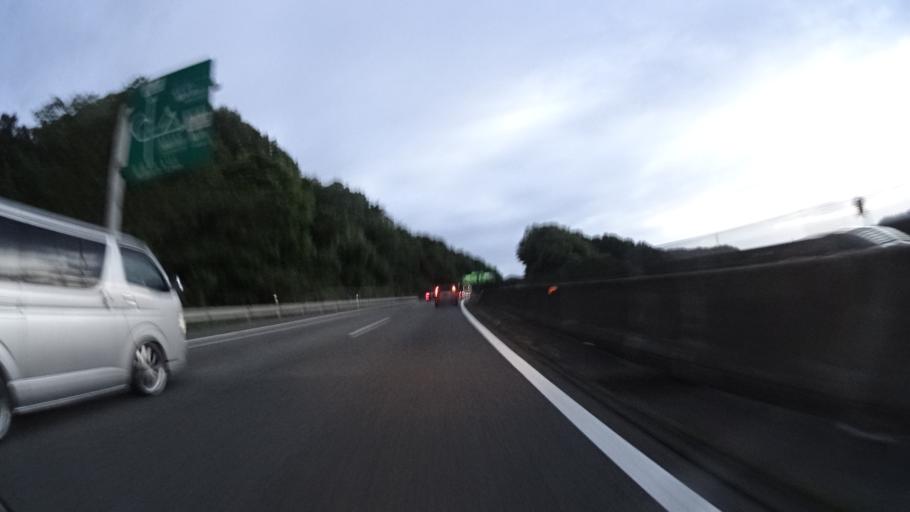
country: JP
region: Shiga Prefecture
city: Nagahama
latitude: 35.3200
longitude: 136.3352
